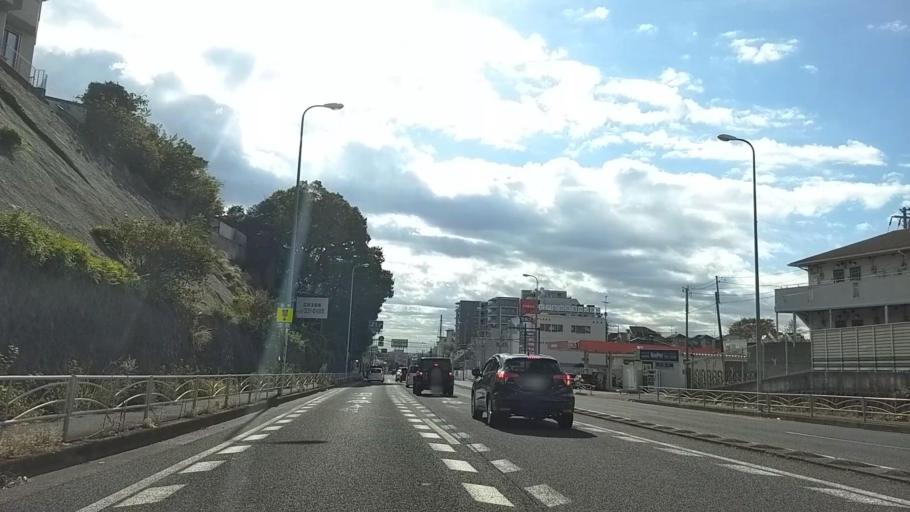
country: JP
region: Kanagawa
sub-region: Kawasaki-shi
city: Kawasaki
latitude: 35.5035
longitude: 139.6622
